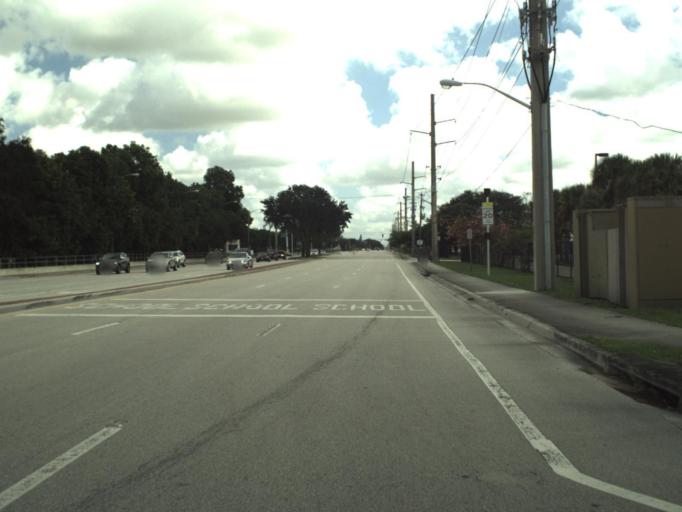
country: US
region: Florida
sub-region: Palm Beach County
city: Boca Del Mar
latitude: 26.3944
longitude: -80.1460
